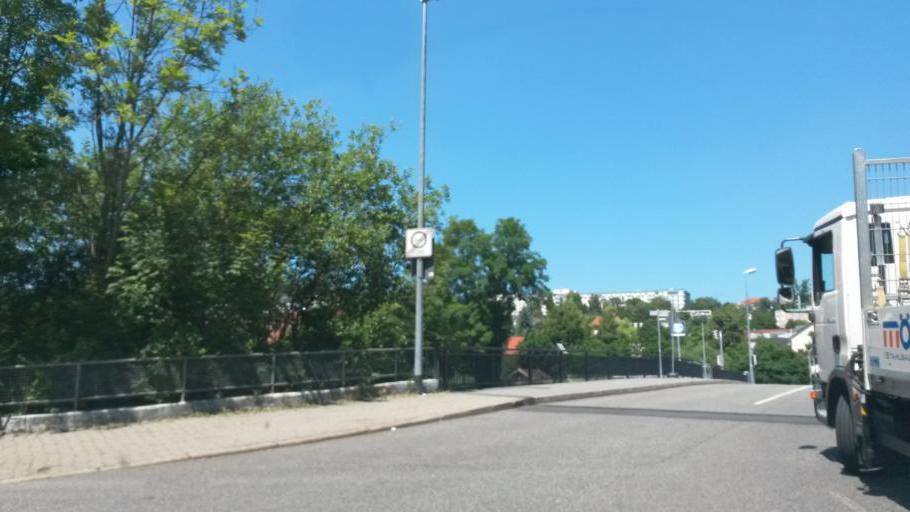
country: DE
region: Baden-Wuerttemberg
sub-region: Karlsruhe Region
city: Pforzheim
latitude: 48.8931
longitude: 8.6790
